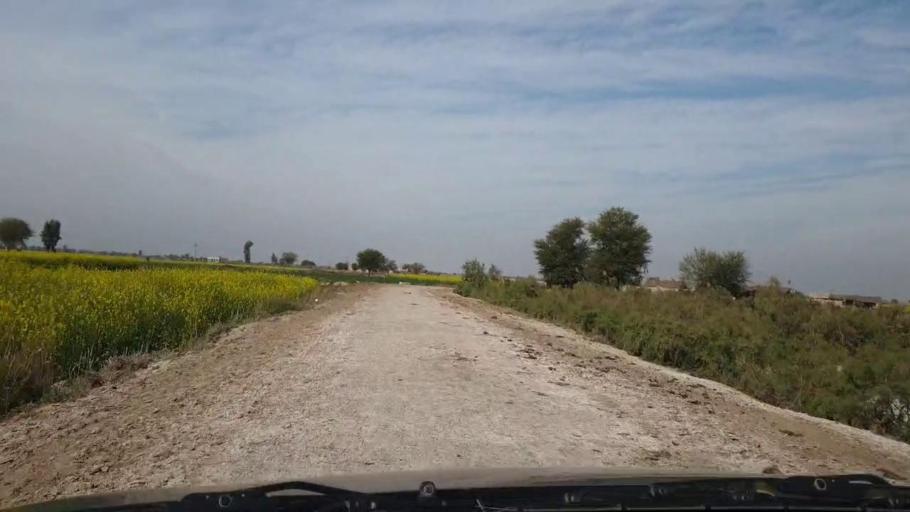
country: PK
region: Sindh
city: Jam Sahib
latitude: 26.2710
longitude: 68.7092
